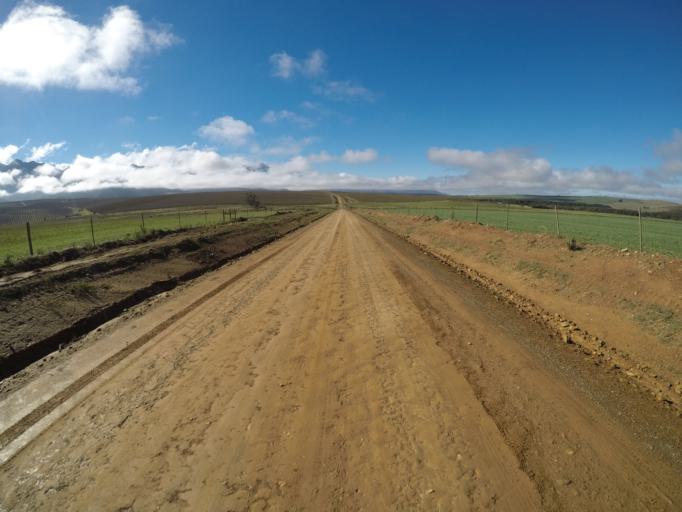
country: ZA
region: Western Cape
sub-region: Overberg District Municipality
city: Caledon
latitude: -34.1200
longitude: 19.7287
